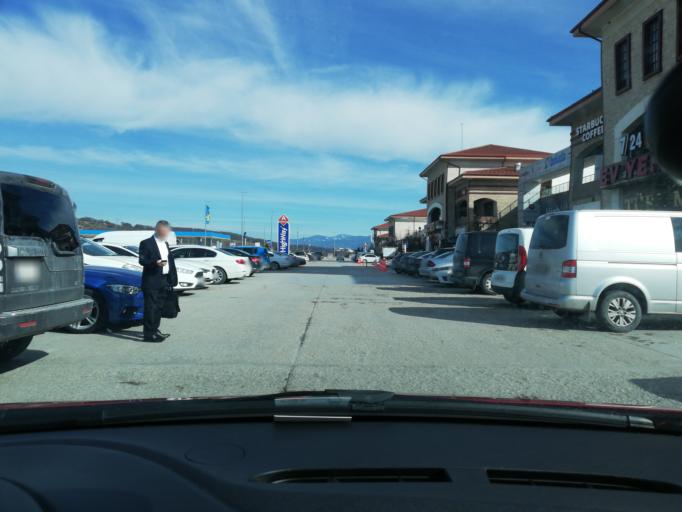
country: TR
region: Bolu
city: Bolu
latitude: 40.7230
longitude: 31.4657
